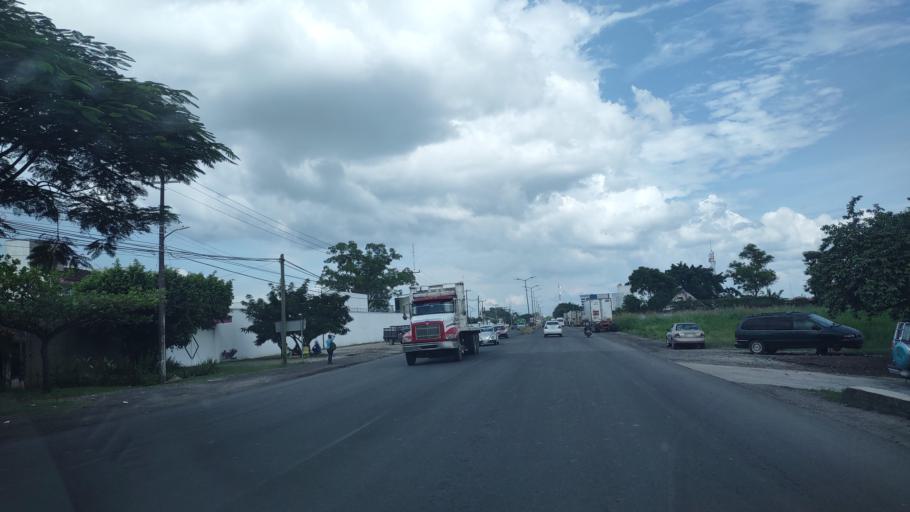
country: MX
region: Veracruz
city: Martinez de la Torre
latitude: 20.0692
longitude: -97.0719
